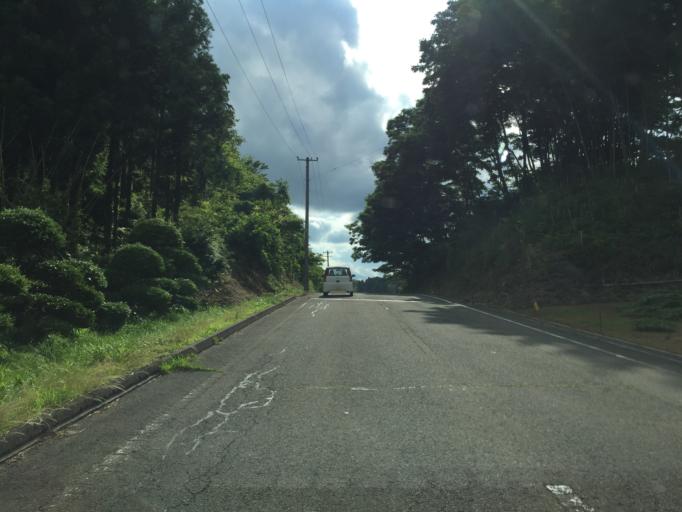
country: JP
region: Fukushima
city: Fukushima-shi
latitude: 37.6694
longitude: 140.5439
